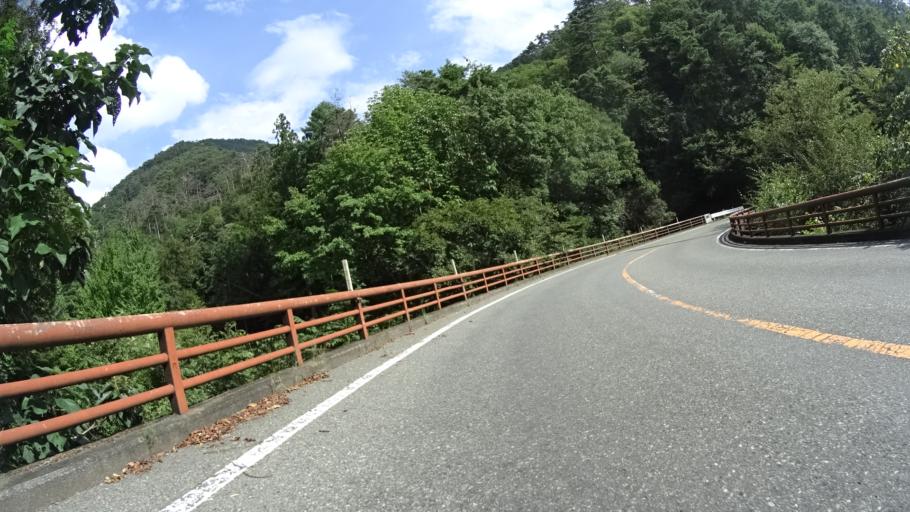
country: JP
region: Yamanashi
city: Kofu-shi
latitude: 35.7235
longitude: 138.5592
